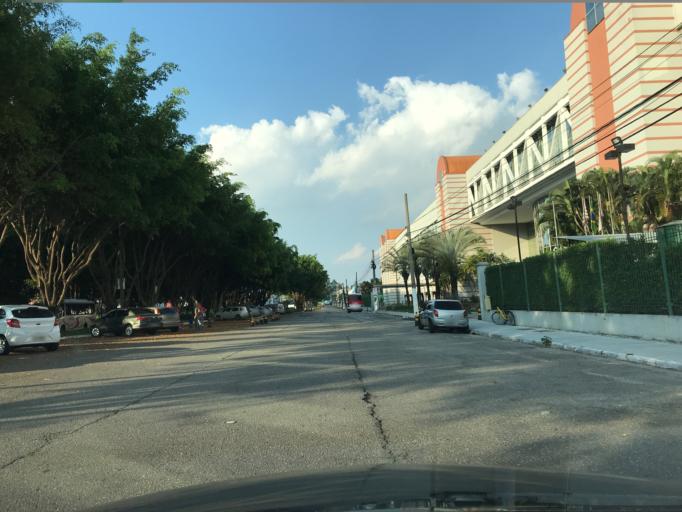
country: BR
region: Sao Paulo
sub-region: Osasco
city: Osasco
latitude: -23.5266
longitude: -46.7456
